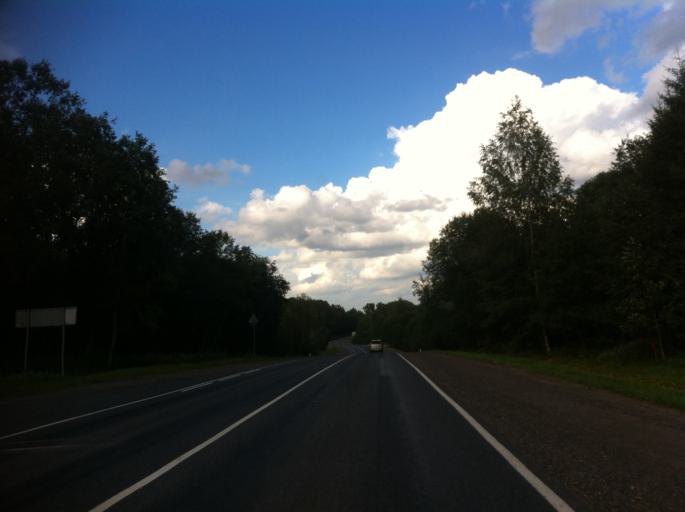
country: RU
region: Pskov
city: Strugi-Krasnyye
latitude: 58.1921
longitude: 29.2797
